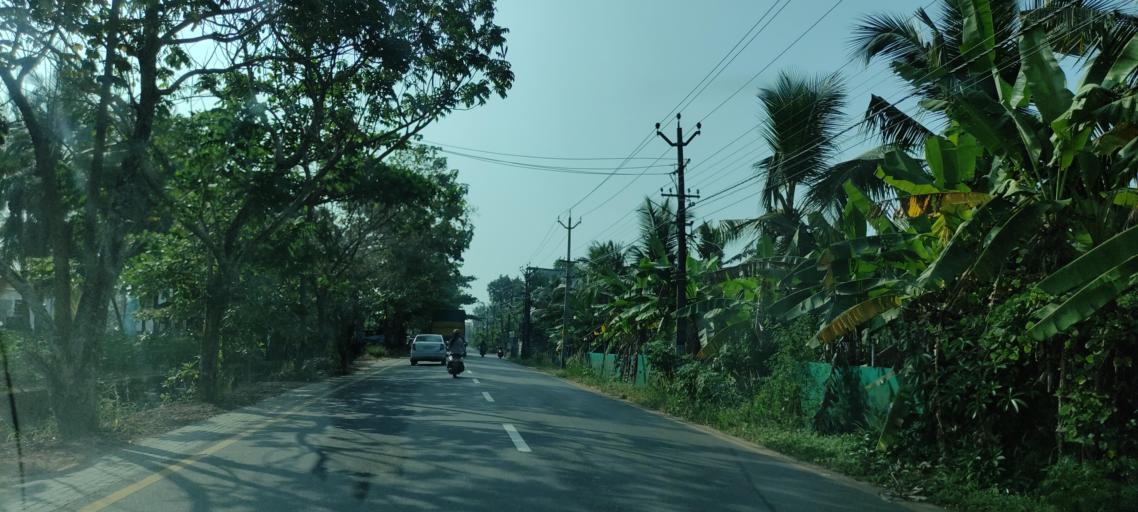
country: IN
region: Kerala
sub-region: Kottayam
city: Changanacheri
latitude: 9.3618
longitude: 76.4627
